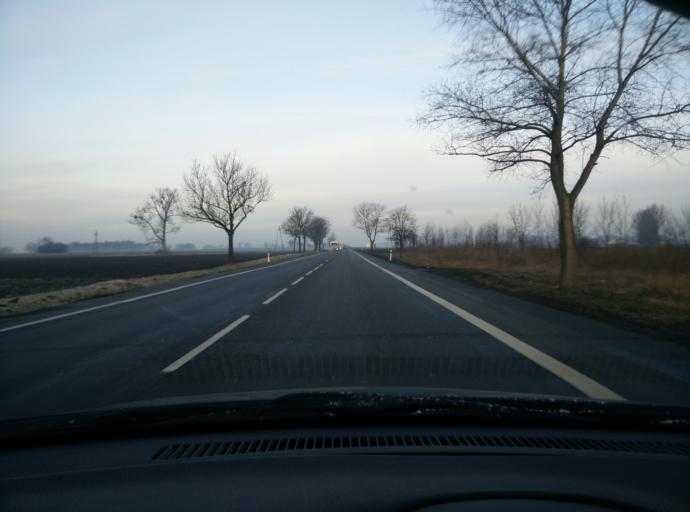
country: PL
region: Greater Poland Voivodeship
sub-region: Powiat poznanski
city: Kornik
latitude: 52.2389
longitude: 17.1547
